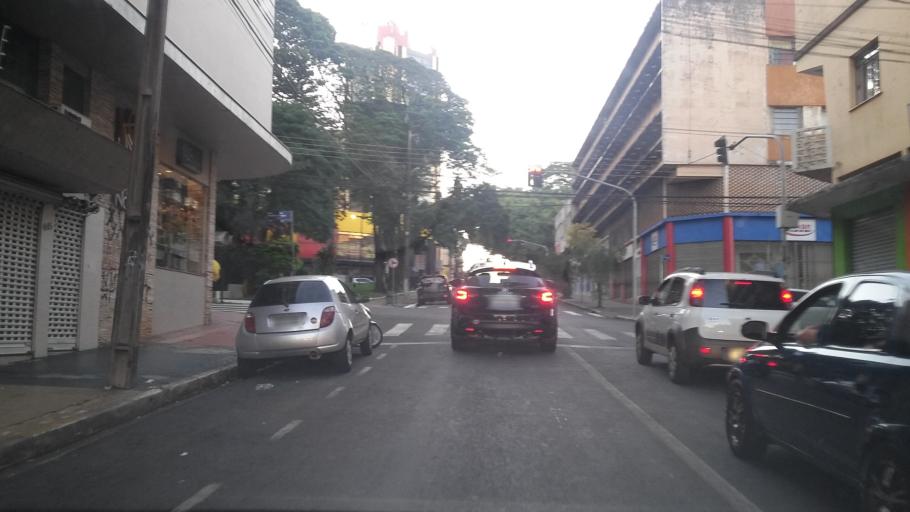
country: BR
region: Parana
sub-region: Londrina
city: Londrina
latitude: -23.3098
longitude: -51.1637
